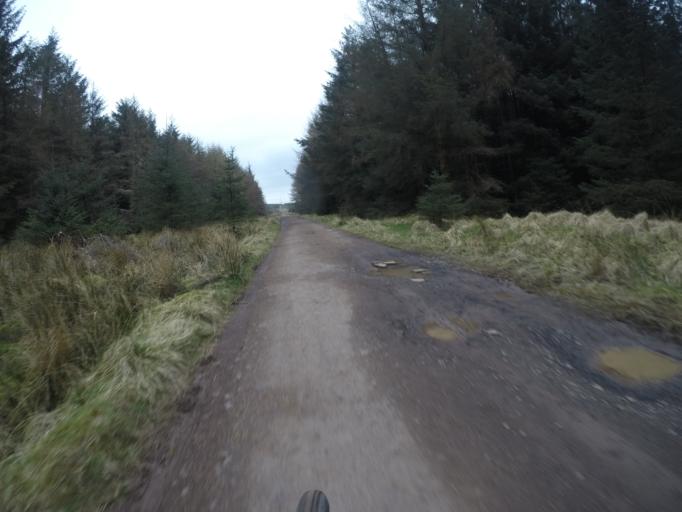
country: GB
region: Scotland
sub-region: East Ayrshire
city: Newmilns
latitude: 55.6586
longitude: -4.3349
